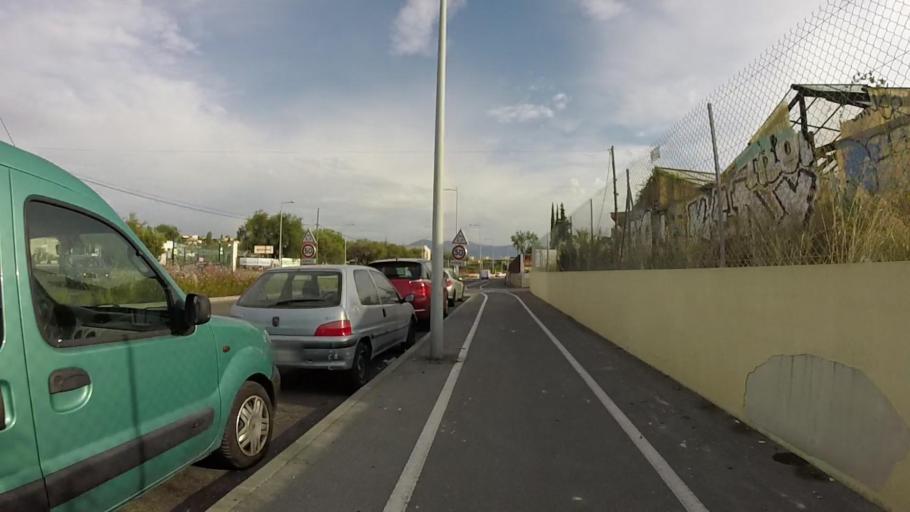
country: FR
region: Provence-Alpes-Cote d'Azur
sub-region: Departement des Alpes-Maritimes
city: Biot
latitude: 43.5983
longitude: 7.1135
